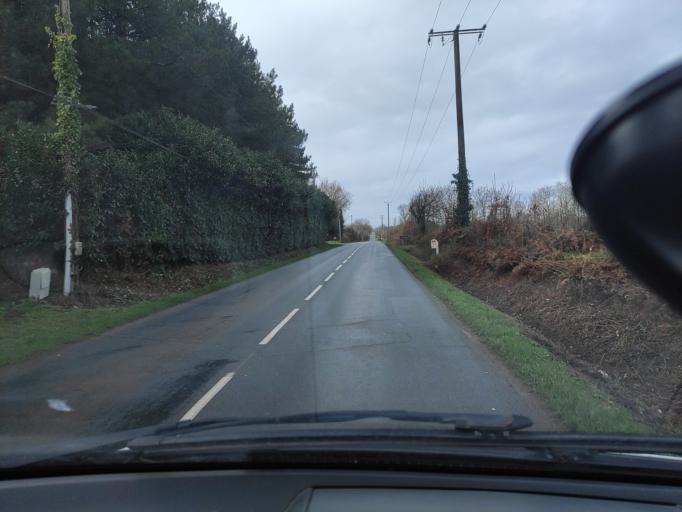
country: FR
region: Pays de la Loire
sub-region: Departement de la Vendee
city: La Boissiere-des-Landes
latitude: 46.5660
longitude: -1.4700
